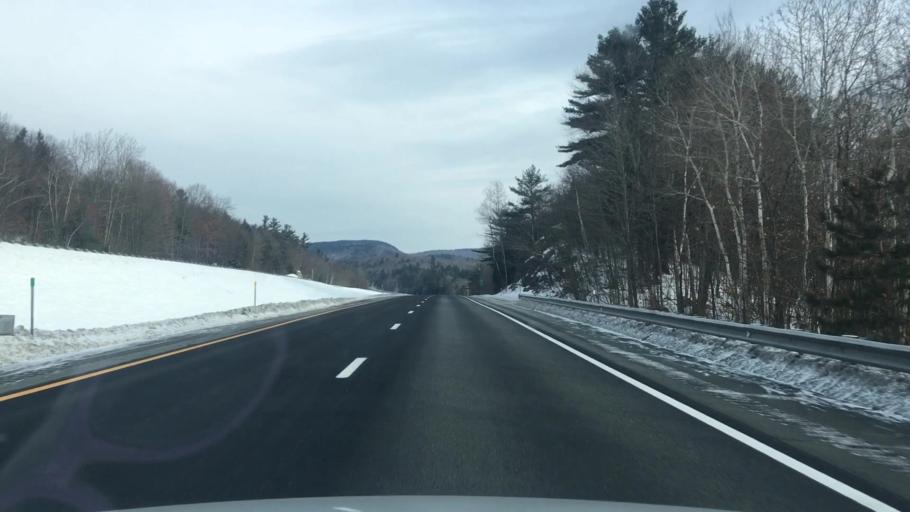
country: US
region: New Hampshire
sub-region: Sullivan County
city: Grantham
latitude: 43.5334
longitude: -72.1392
